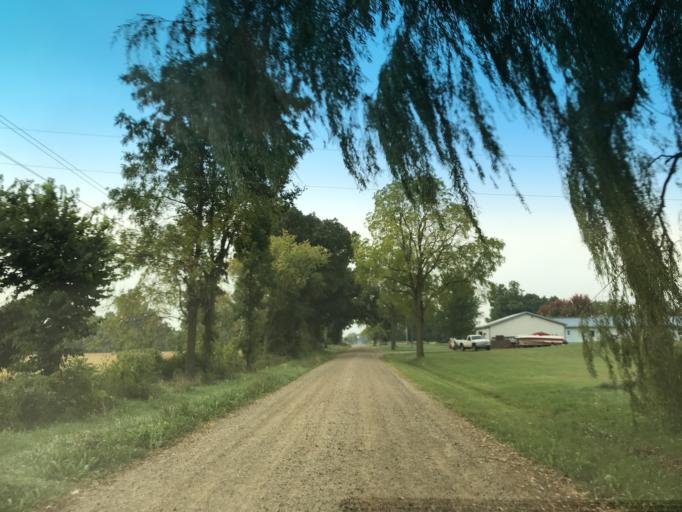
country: US
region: Michigan
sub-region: Eaton County
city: Grand Ledge
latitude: 42.8074
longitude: -84.7788
